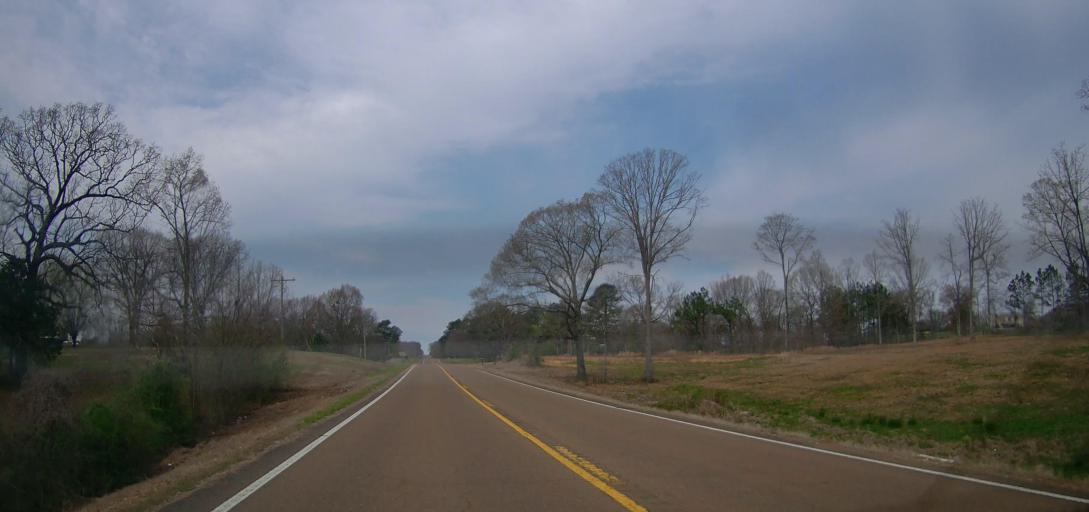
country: US
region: Mississippi
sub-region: Marshall County
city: Byhalia
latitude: 34.8314
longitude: -89.5744
